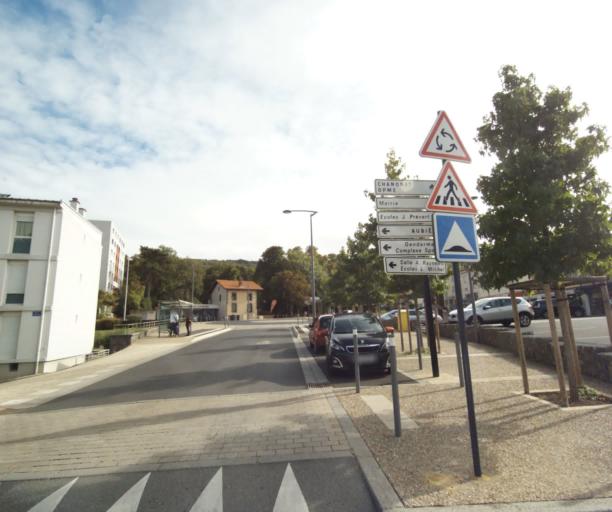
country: FR
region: Auvergne
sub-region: Departement du Puy-de-Dome
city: Romagnat
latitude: 45.7317
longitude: 3.0995
